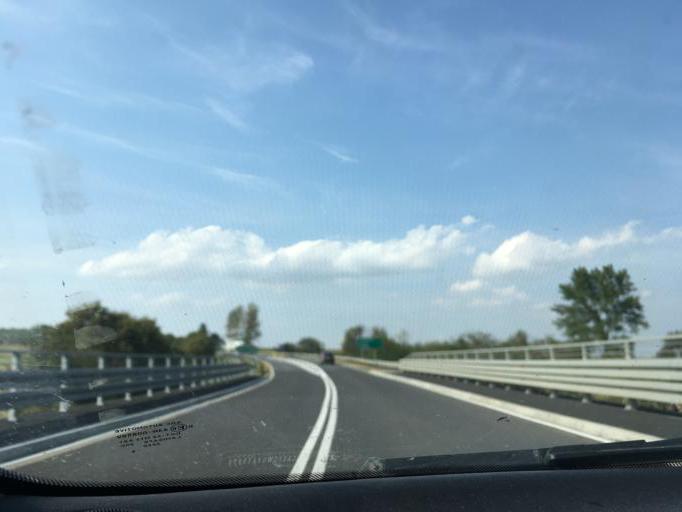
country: PL
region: Opole Voivodeship
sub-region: Powiat prudnicki
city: Laka Prudnicka
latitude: 50.4061
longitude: 17.5095
